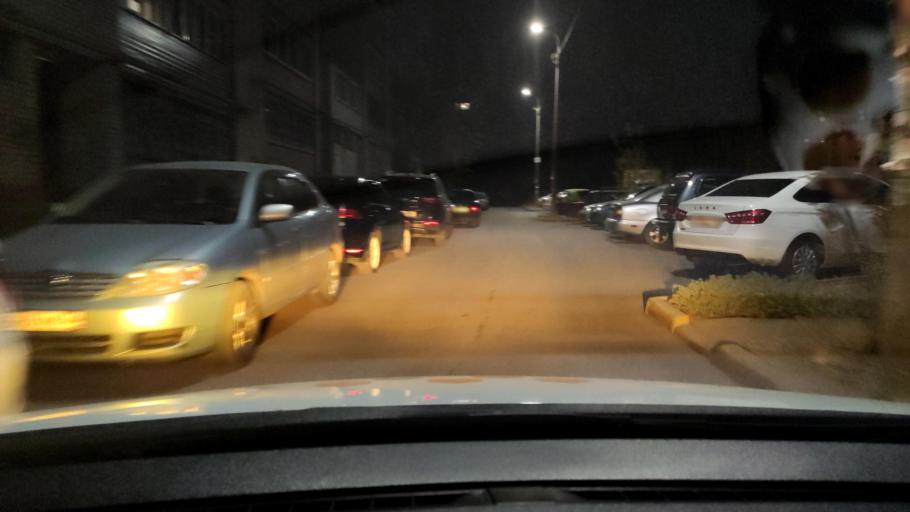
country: RU
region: Voronezj
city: Podgornoye
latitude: 51.6907
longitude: 39.1314
